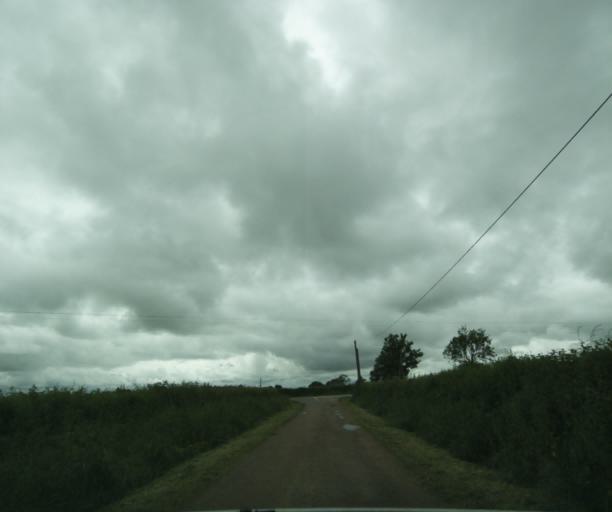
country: FR
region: Bourgogne
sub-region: Departement de Saone-et-Loire
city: Charolles
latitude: 46.4683
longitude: 4.2764
